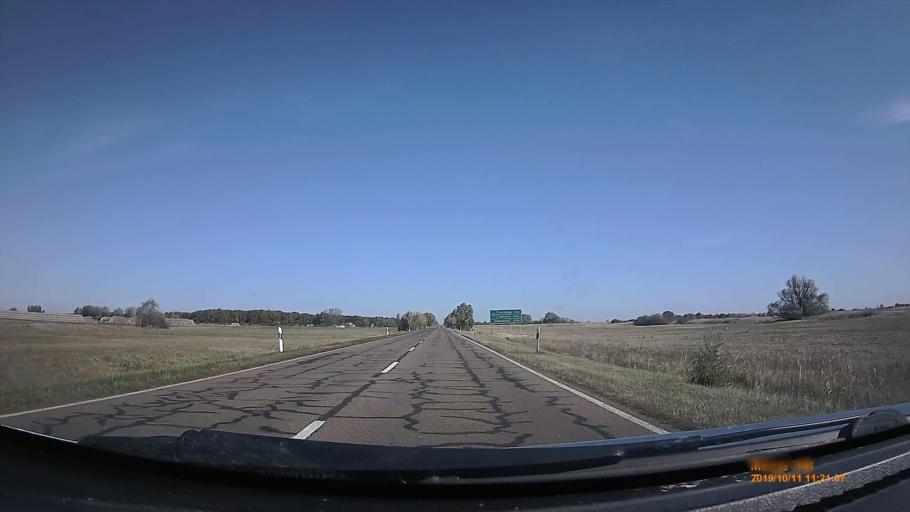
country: HU
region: Hajdu-Bihar
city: Egyek
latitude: 47.5741
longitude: 20.9926
